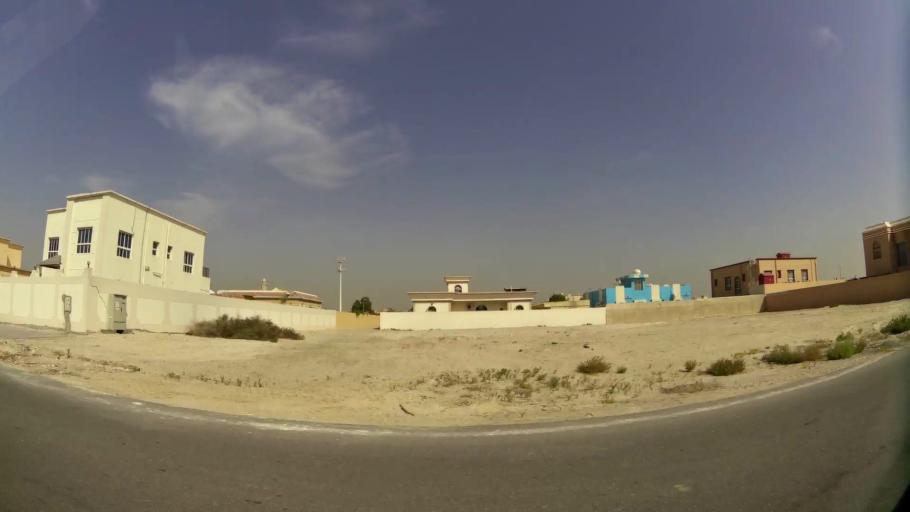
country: AE
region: Ash Shariqah
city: Sharjah
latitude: 25.2681
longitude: 55.4052
